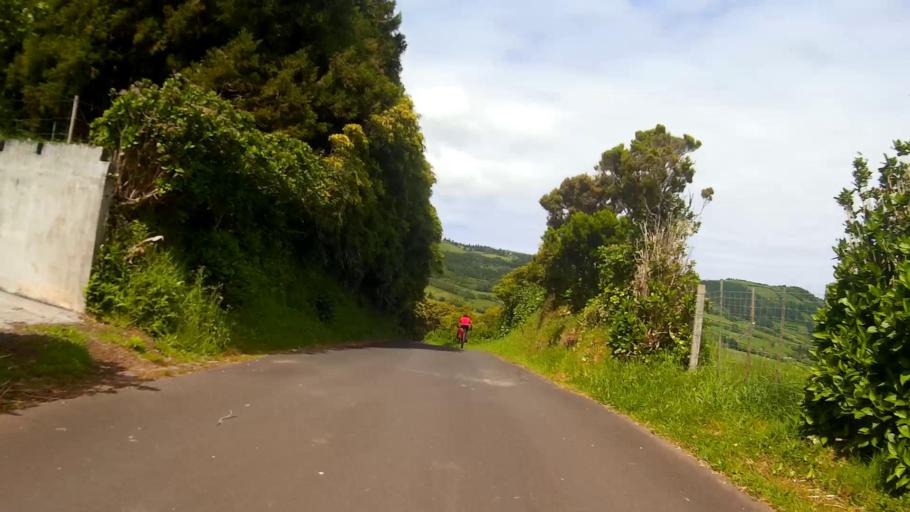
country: PT
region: Azores
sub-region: Horta
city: Horta
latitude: 38.5513
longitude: -28.6699
